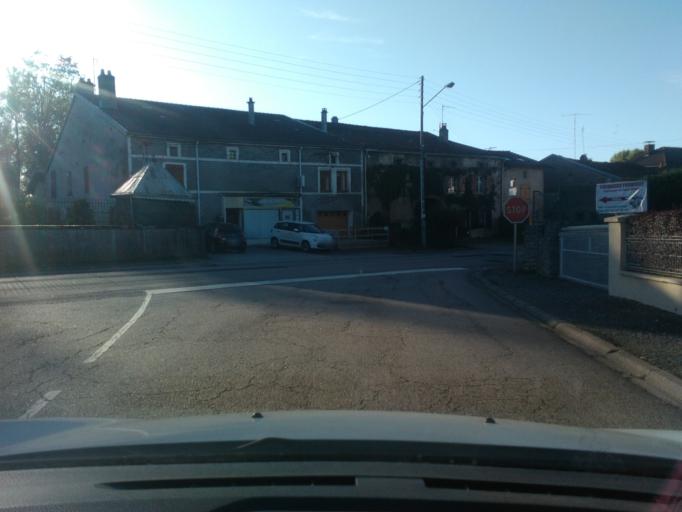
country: FR
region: Lorraine
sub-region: Departement des Vosges
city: Jeanmenil
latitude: 48.2889
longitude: 6.6585
